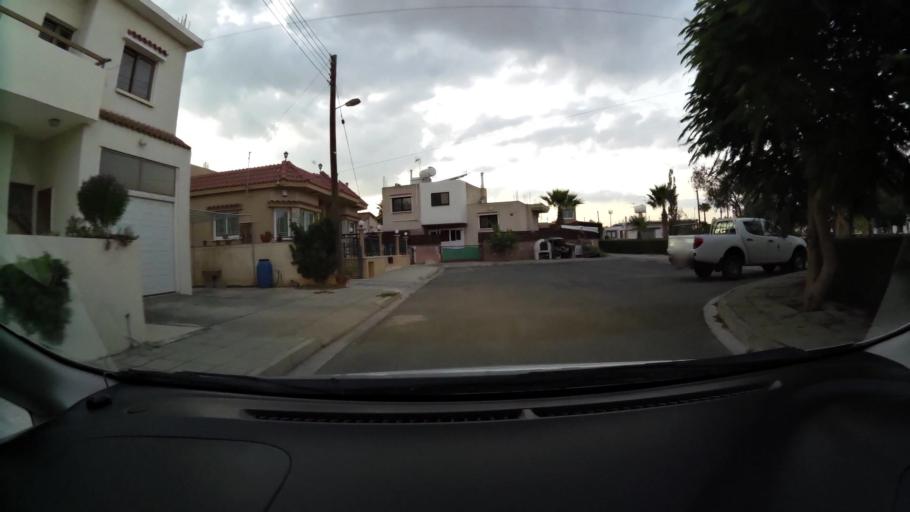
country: CY
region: Larnaka
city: Dhromolaxia
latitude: 34.8735
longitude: 33.5815
